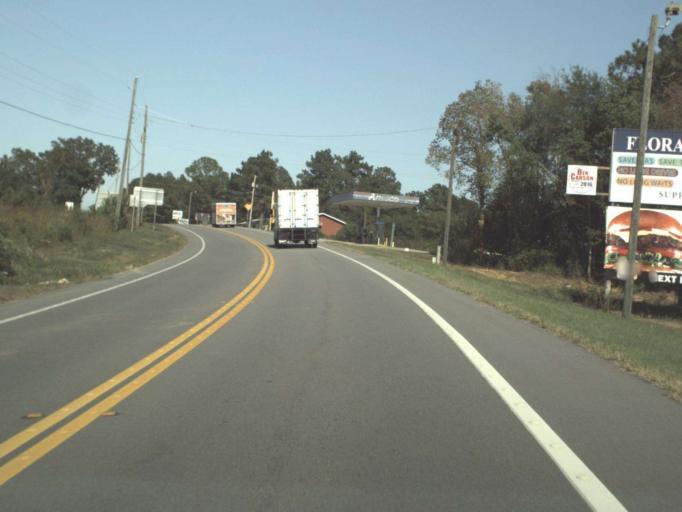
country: US
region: Alabama
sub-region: Covington County
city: Florala
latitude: 30.9916
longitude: -86.3363
